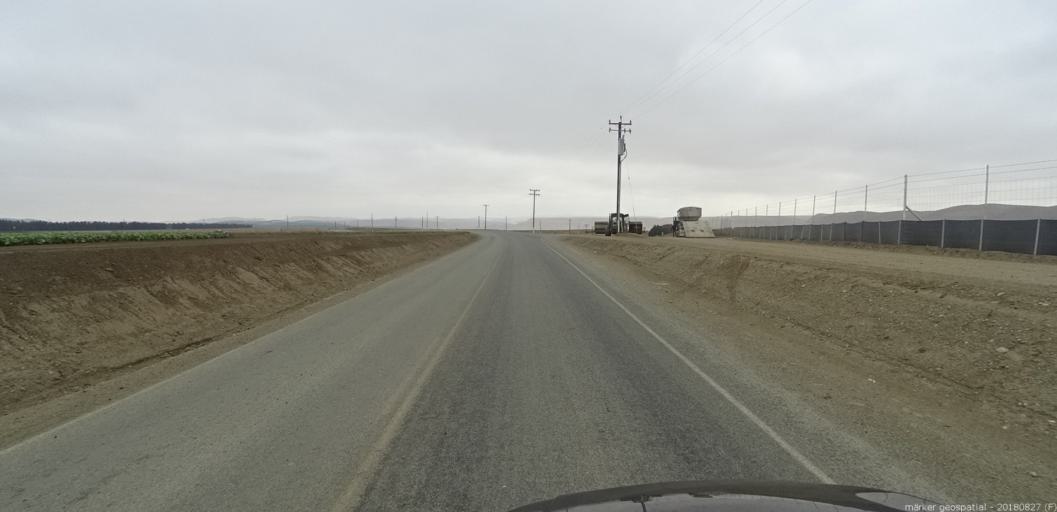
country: US
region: California
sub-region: Monterey County
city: King City
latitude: 36.2306
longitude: -121.1070
